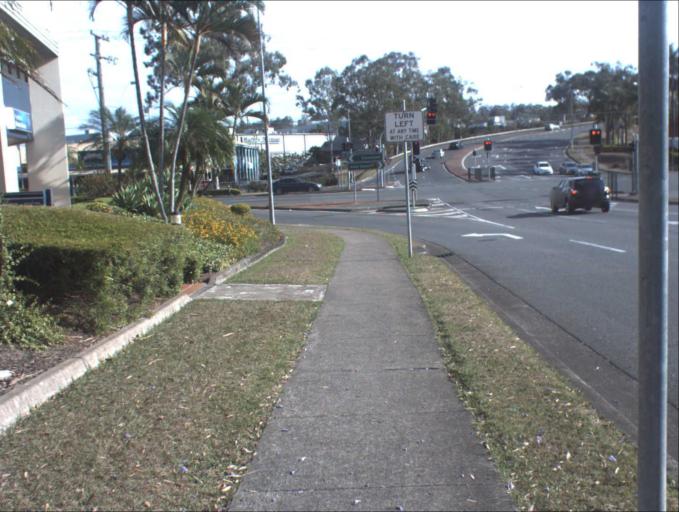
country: AU
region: Queensland
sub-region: Logan
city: Slacks Creek
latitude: -27.6620
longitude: 153.1748
